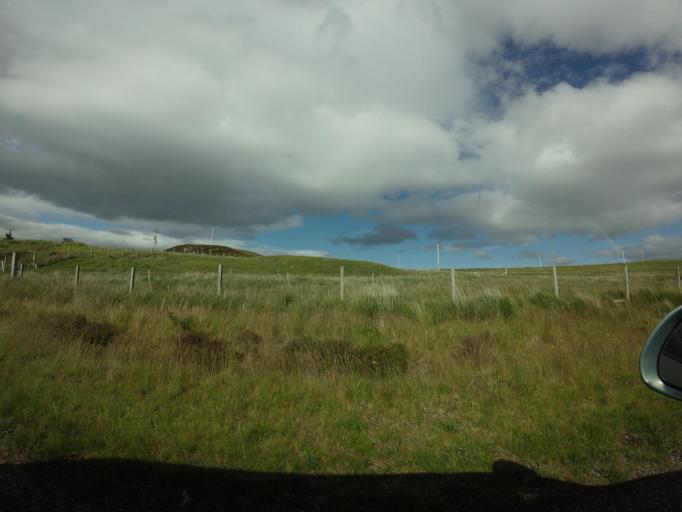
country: GB
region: Scotland
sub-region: Eilean Siar
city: Harris
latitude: 58.1914
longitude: -6.7083
